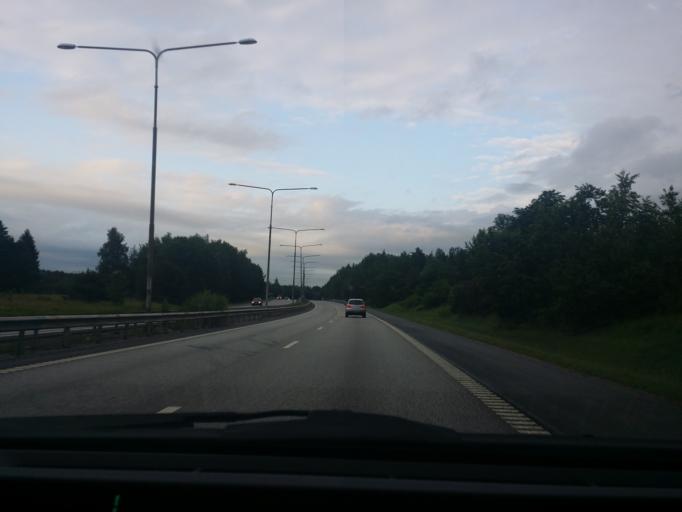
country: SE
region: Vaestmanland
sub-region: Vasteras
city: Vasteras
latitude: 59.6136
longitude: 16.4886
